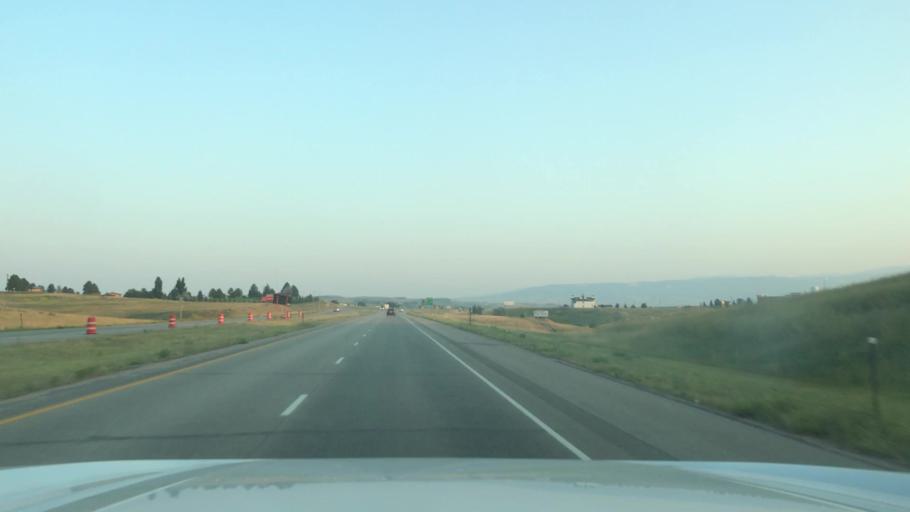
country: US
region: Wyoming
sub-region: Sheridan County
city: Sheridan
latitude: 44.8126
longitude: -106.9385
